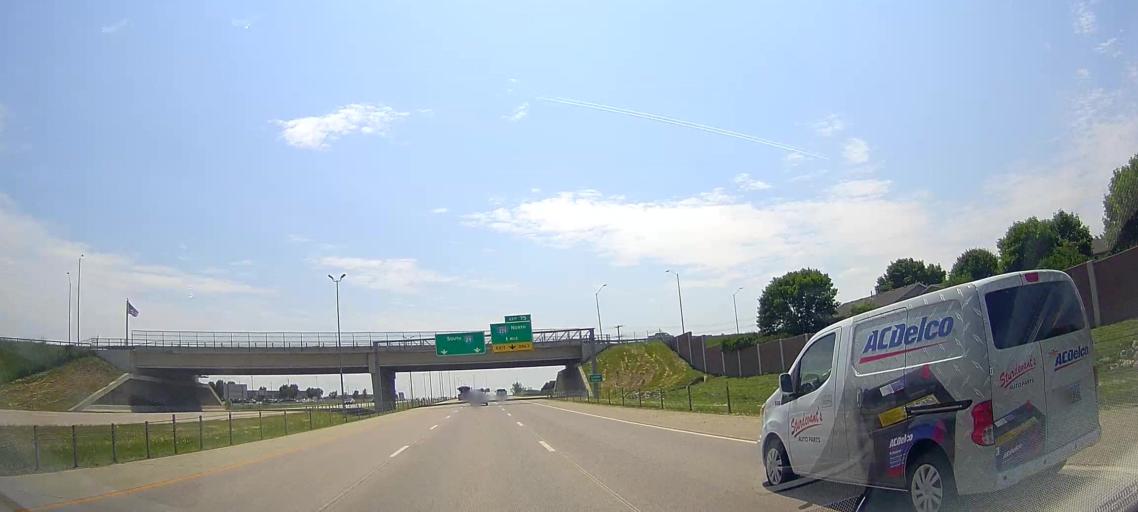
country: US
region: South Dakota
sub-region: Lincoln County
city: Tea
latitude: 43.5009
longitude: -96.7879
